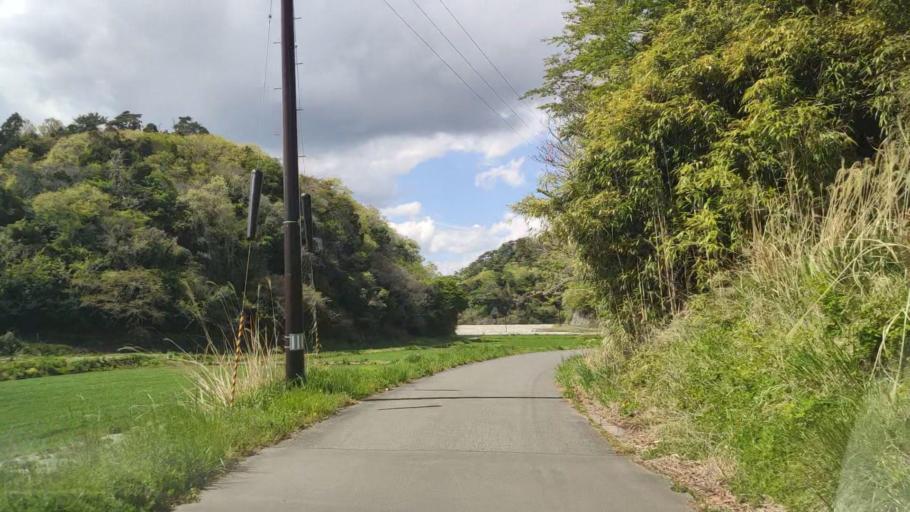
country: JP
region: Miyagi
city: Yamoto
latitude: 38.3378
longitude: 141.1644
